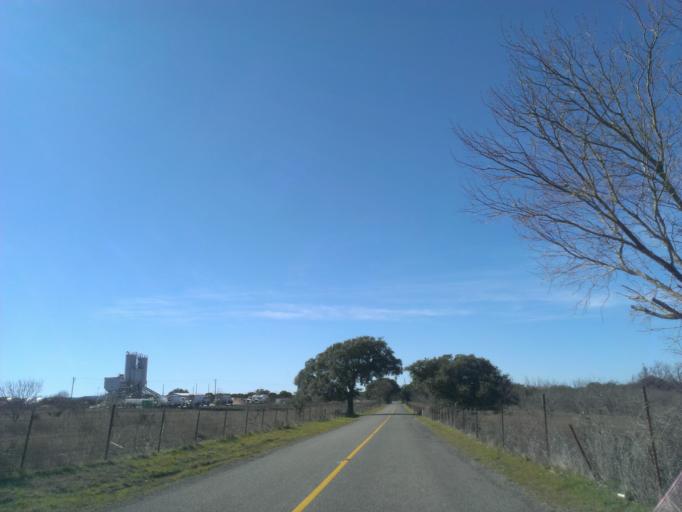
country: US
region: Texas
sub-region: Burnet County
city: Marble Falls
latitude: 30.4748
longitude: -98.1792
